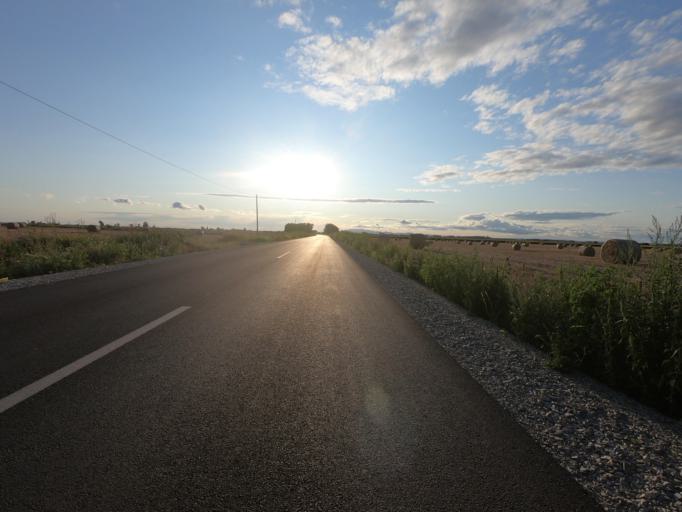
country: HU
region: Heves
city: Szihalom
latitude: 47.7091
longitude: 20.5097
